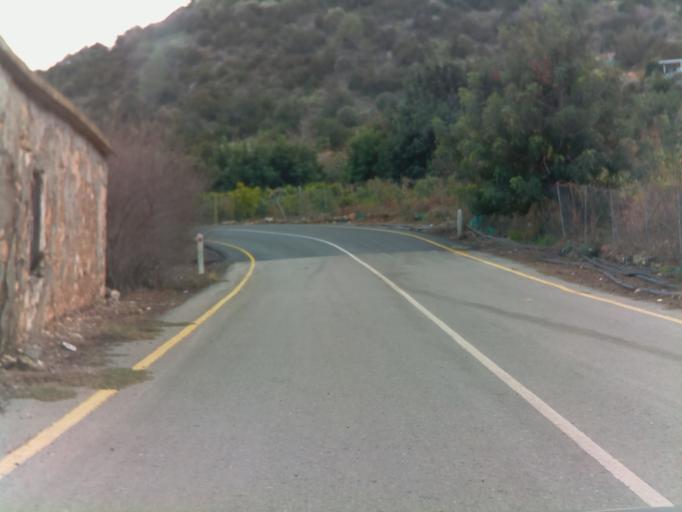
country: CY
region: Pafos
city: Polis
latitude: 35.0545
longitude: 32.3476
